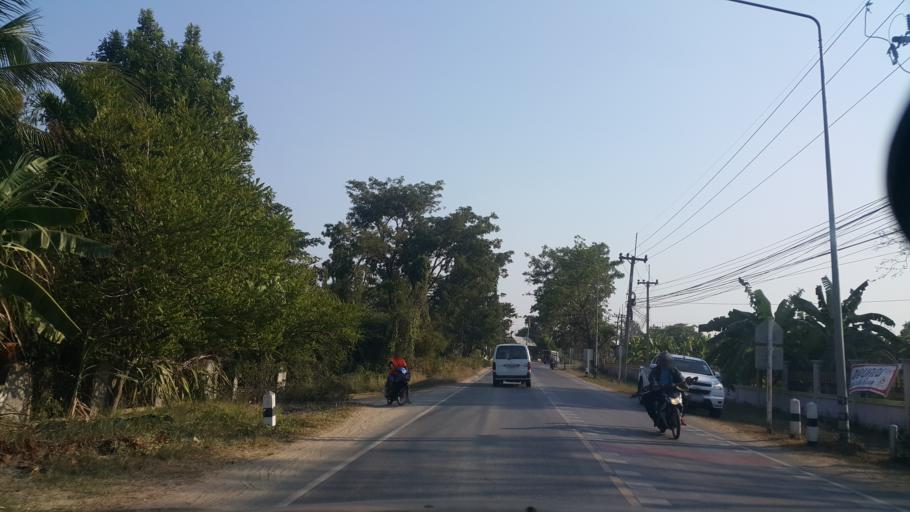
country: TH
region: Nakhon Ratchasima
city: Chakkarat
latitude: 15.0689
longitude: 102.3947
